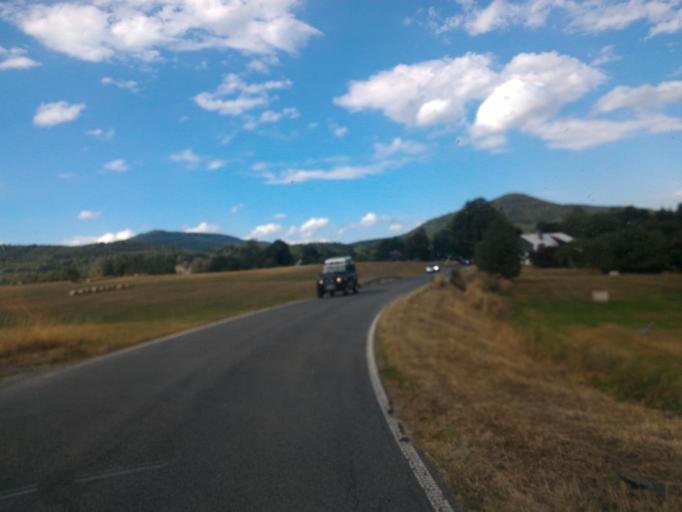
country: CZ
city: Jablonne v Podjestedi
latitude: 50.7872
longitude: 14.7333
